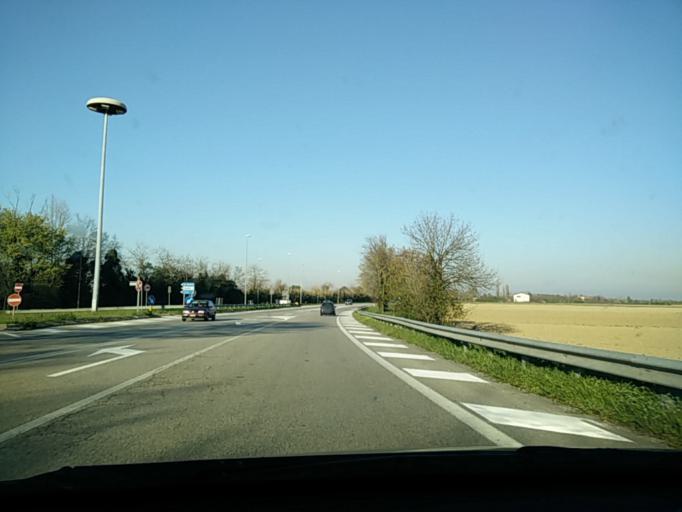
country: IT
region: Veneto
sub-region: Provincia di Venezia
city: San Liberale
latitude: 45.5248
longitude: 12.3696
